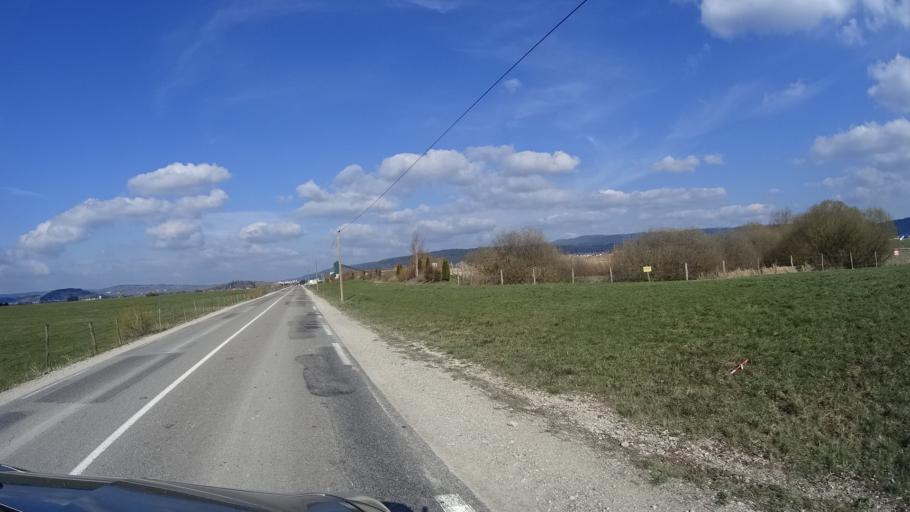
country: FR
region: Franche-Comte
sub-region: Departement du Doubs
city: Doubs
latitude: 46.9179
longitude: 6.3218
